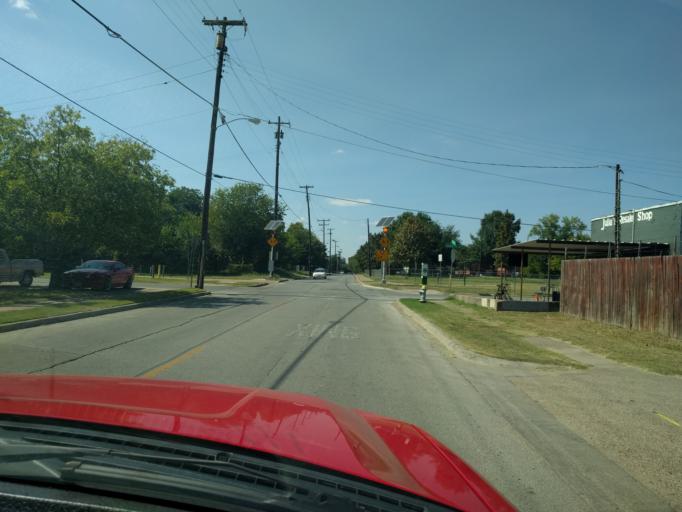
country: US
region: Texas
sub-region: Dallas County
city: Dallas
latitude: 32.7931
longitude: -96.7612
